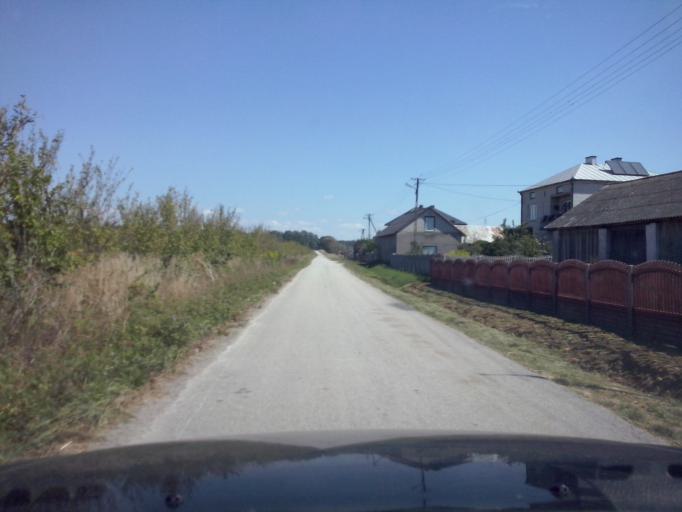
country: PL
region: Swietokrzyskie
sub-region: Powiat buski
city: Gnojno
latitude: 50.6032
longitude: 20.9170
